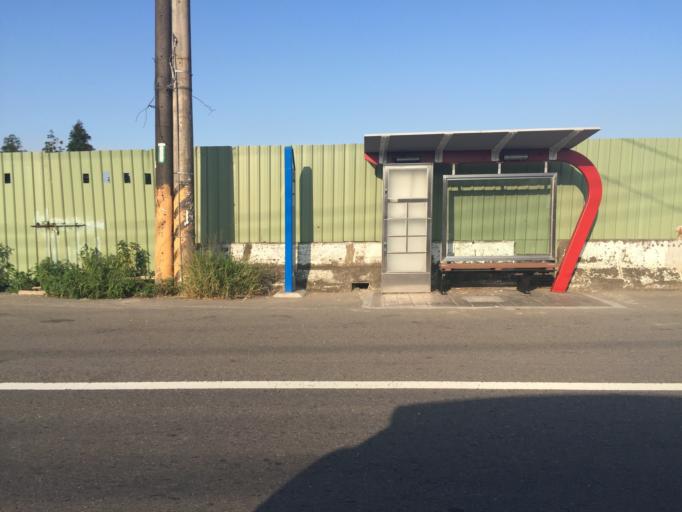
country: TW
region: Taiwan
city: Daxi
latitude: 24.9114
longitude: 121.2543
